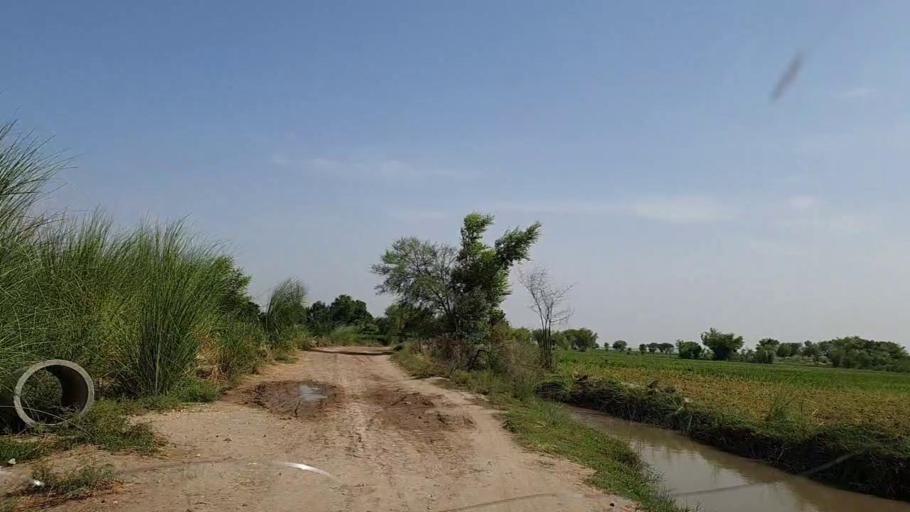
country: PK
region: Sindh
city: Khanpur
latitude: 27.6943
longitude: 69.3668
